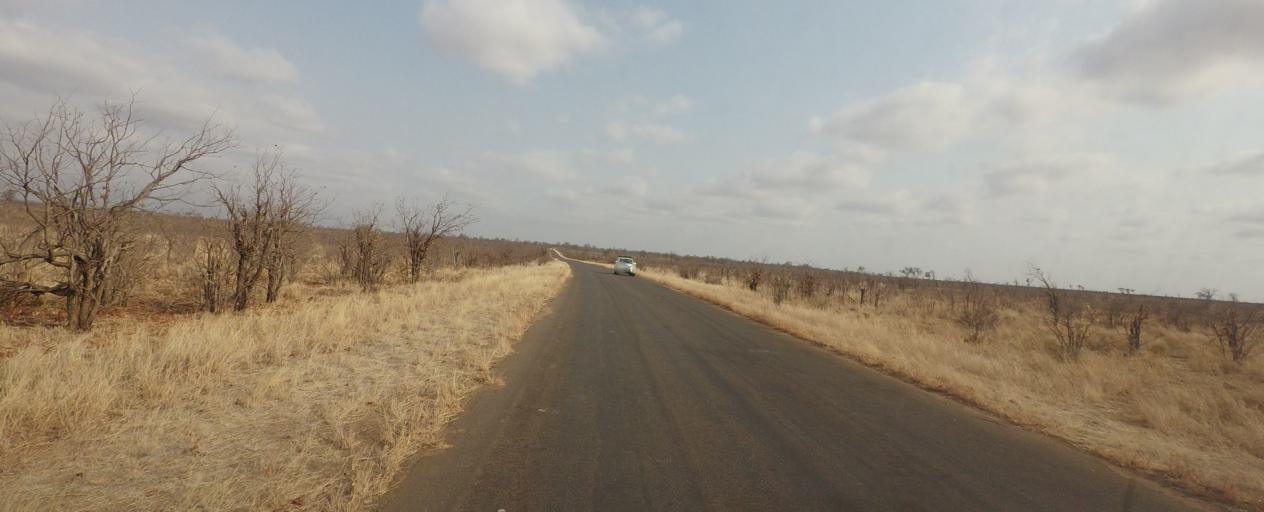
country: ZA
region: Limpopo
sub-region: Vhembe District Municipality
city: Mutale
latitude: -22.8965
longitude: 31.2511
